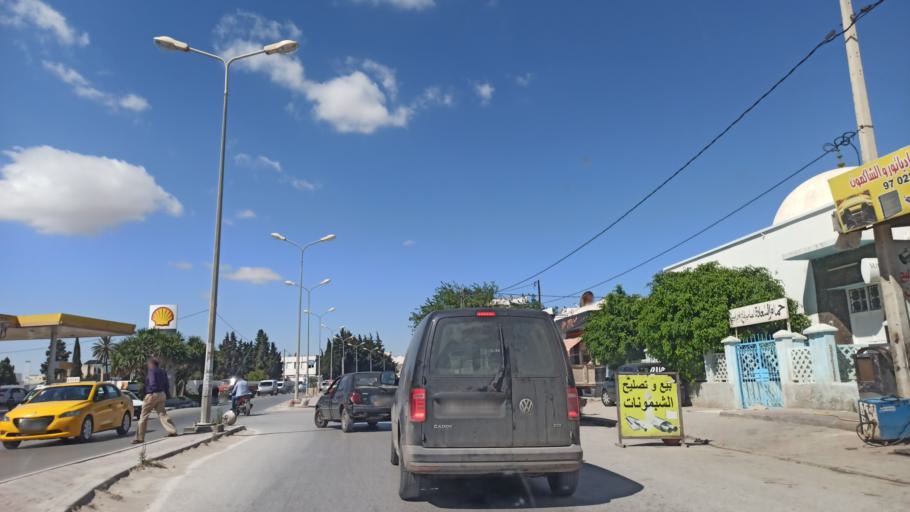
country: TN
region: Manouba
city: Manouba
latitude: 36.7971
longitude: 10.1024
